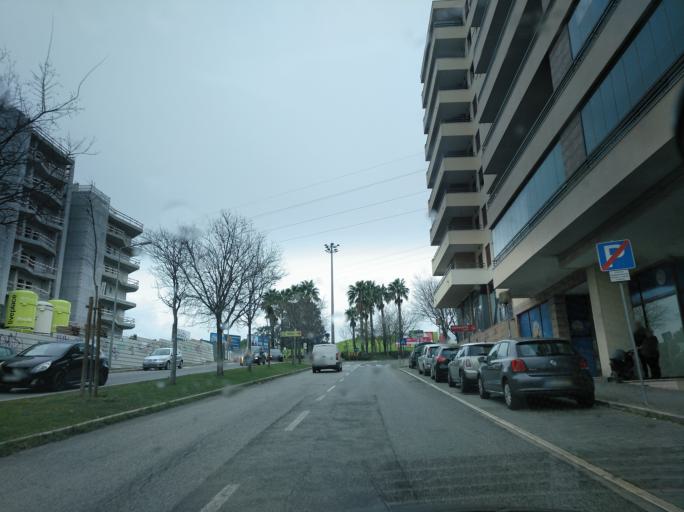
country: PT
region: Lisbon
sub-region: Odivelas
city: Odivelas
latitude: 38.7896
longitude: -9.1946
